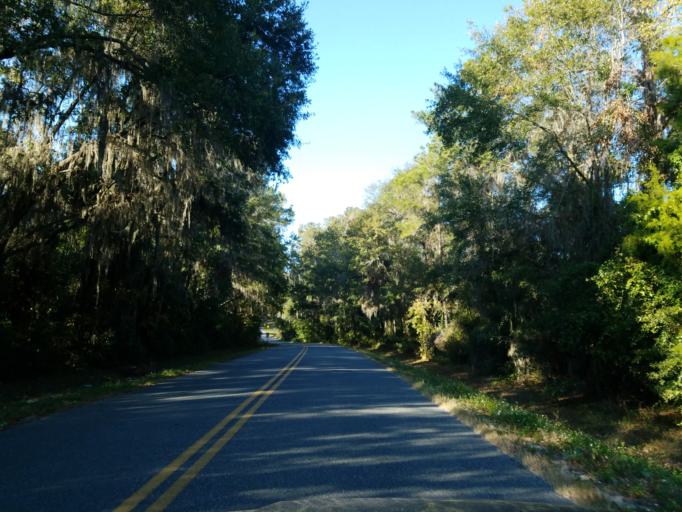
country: US
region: Georgia
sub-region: Echols County
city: Statenville
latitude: 30.6196
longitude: -83.0970
